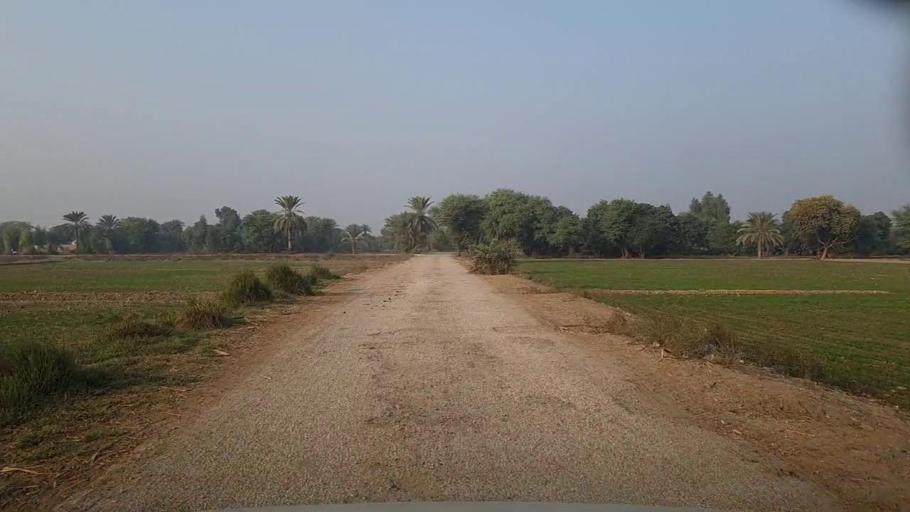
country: PK
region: Sindh
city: Kandiari
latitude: 27.0092
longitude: 68.4613
